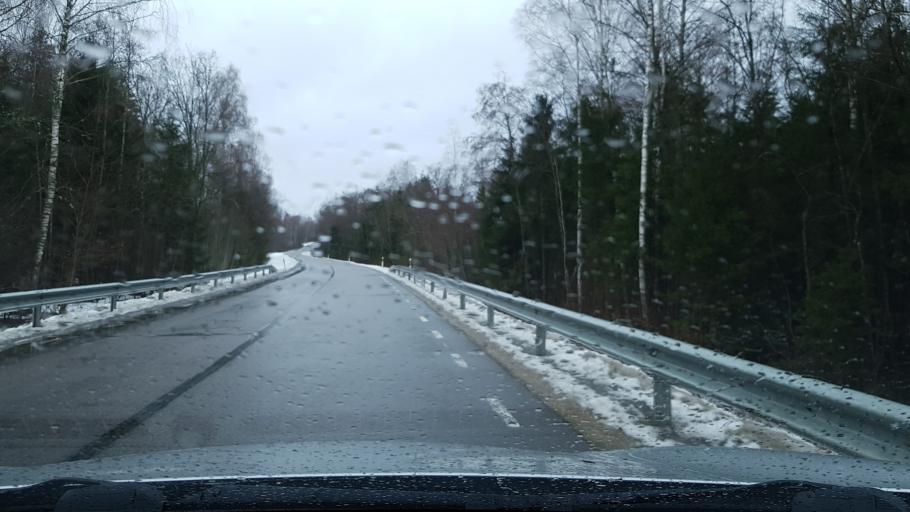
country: LV
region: Apes Novads
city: Ape
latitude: 57.5811
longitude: 26.6561
